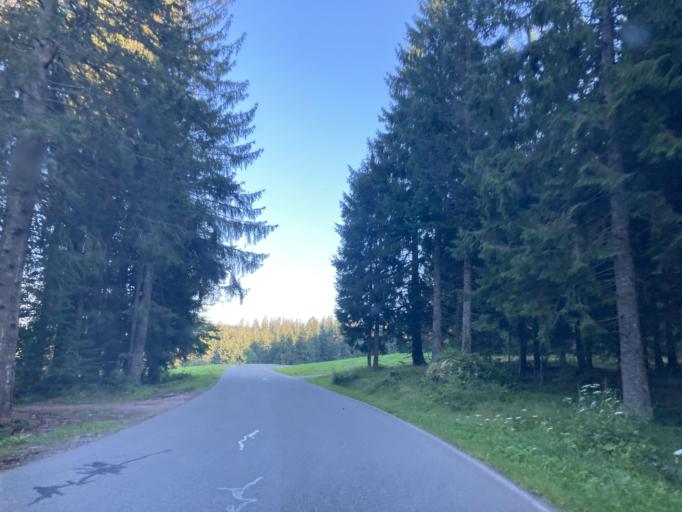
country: DE
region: Baden-Wuerttemberg
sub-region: Freiburg Region
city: Schonach im Schwarzwald
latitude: 48.1587
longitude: 8.1848
